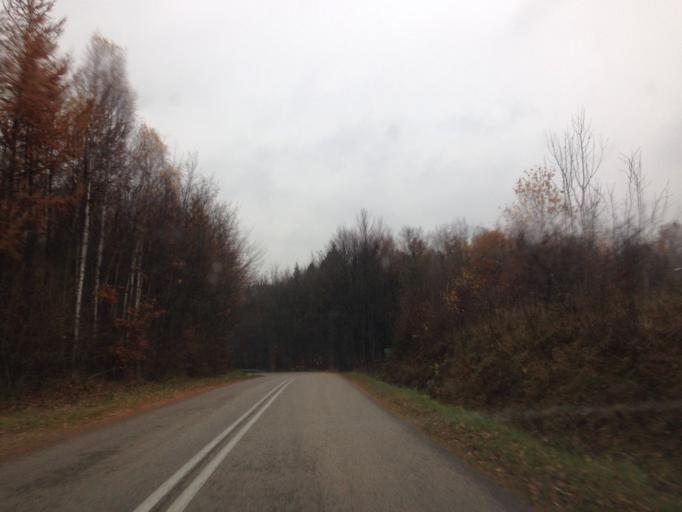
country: PL
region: Pomeranian Voivodeship
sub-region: Powiat gdanski
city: Przywidz
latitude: 54.1928
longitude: 18.3359
